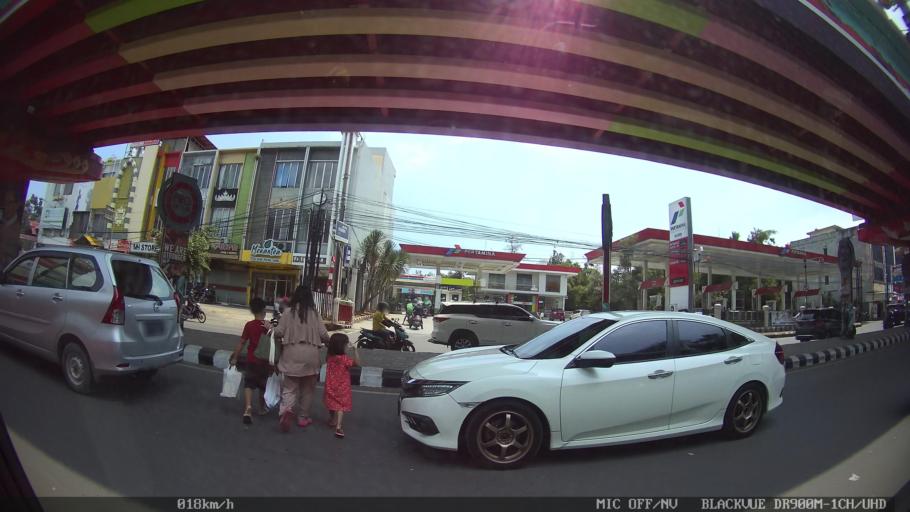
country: ID
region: Lampung
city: Kedaton
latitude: -5.3827
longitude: 105.2592
